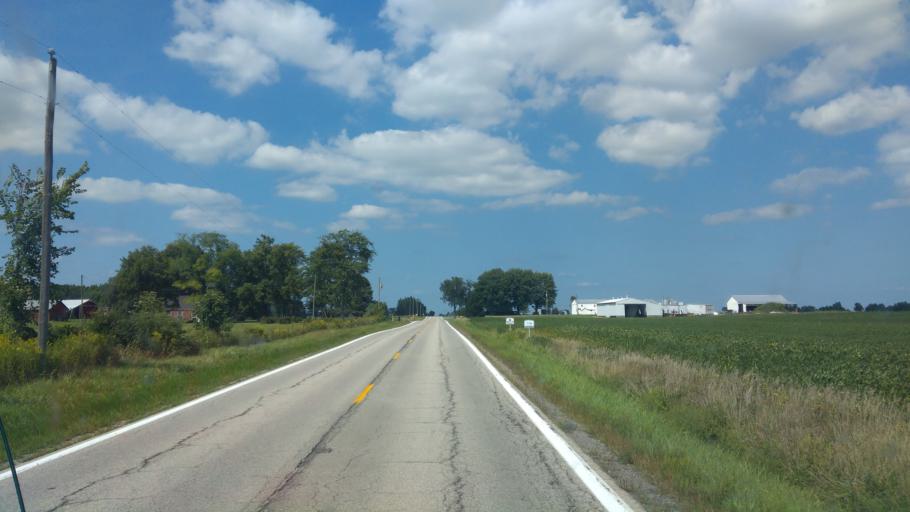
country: US
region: Ohio
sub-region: Union County
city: Marysville
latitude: 40.3652
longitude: -83.4545
